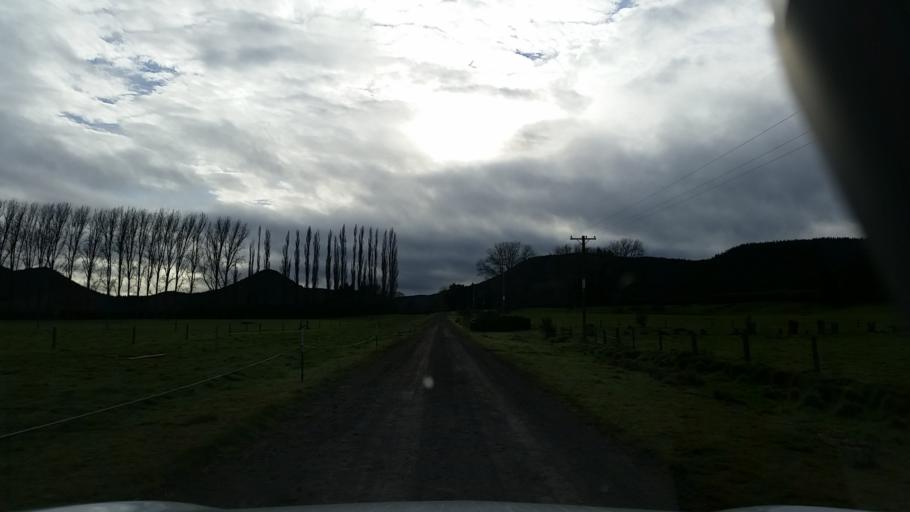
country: NZ
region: Bay of Plenty
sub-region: Rotorua District
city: Rotorua
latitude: -38.3964
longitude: 176.3883
